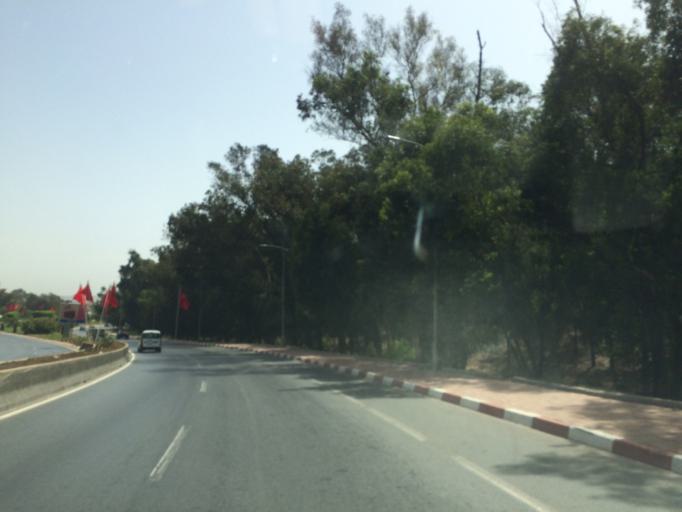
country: MA
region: Rabat-Sale-Zemmour-Zaer
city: Sale
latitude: 34.0272
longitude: -6.7968
